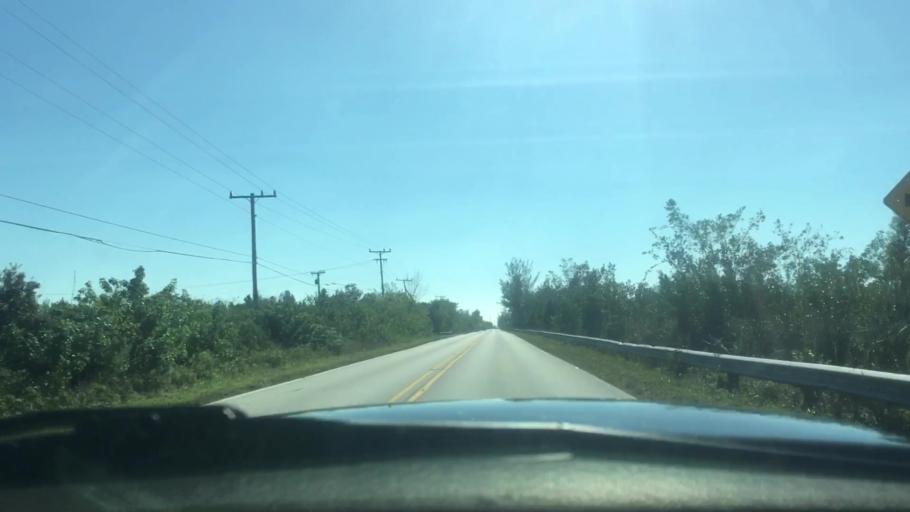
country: US
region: Florida
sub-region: Miami-Dade County
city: Florida City
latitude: 25.3736
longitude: -80.4342
